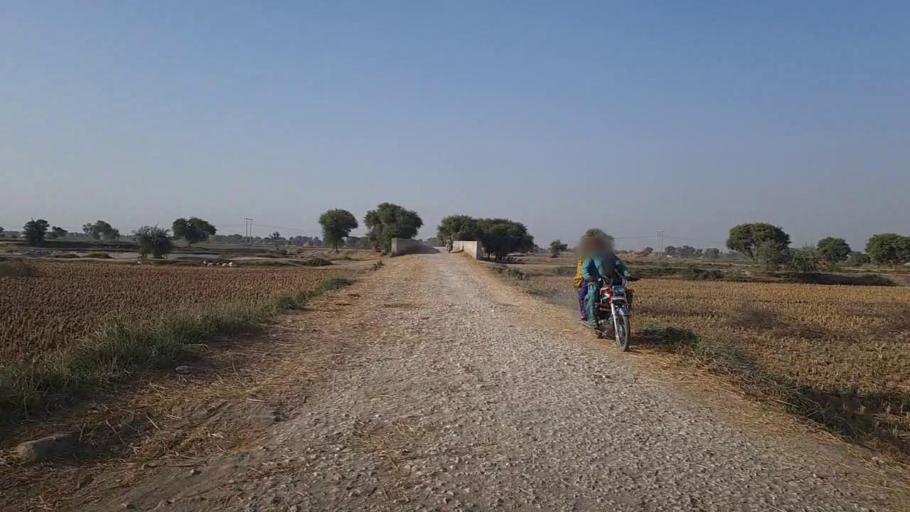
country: PK
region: Sindh
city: Kashmor
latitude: 28.4077
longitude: 69.4130
